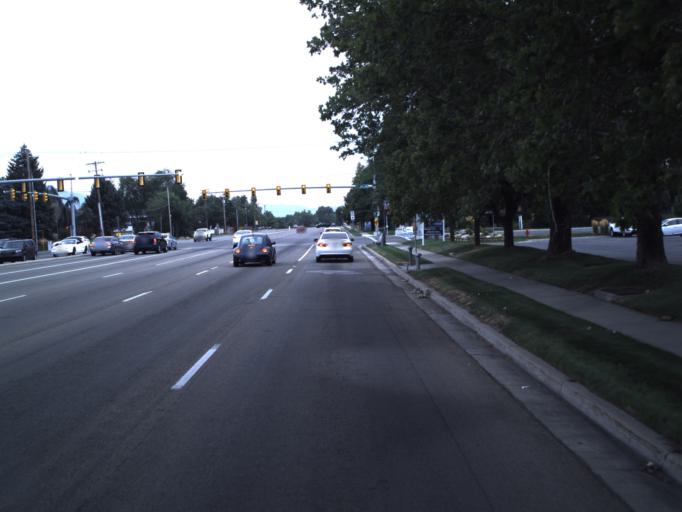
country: US
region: Utah
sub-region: Salt Lake County
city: Millcreek
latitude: 40.6753
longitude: -111.8716
